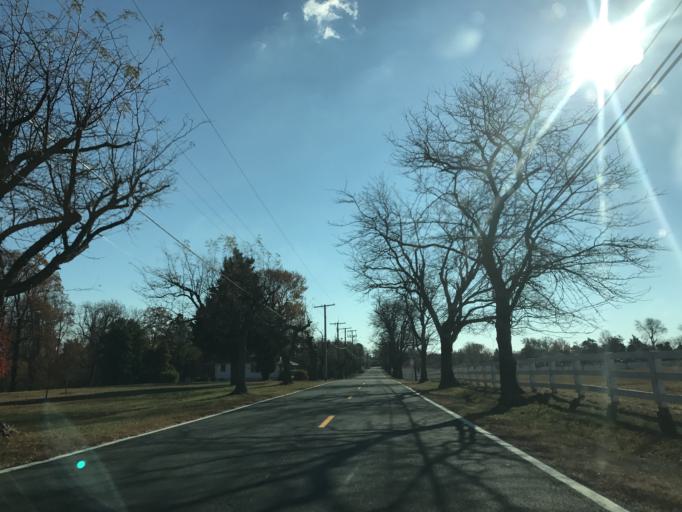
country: US
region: Maryland
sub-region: Anne Arundel County
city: Cape Saint Claire
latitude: 39.0959
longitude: -76.4306
